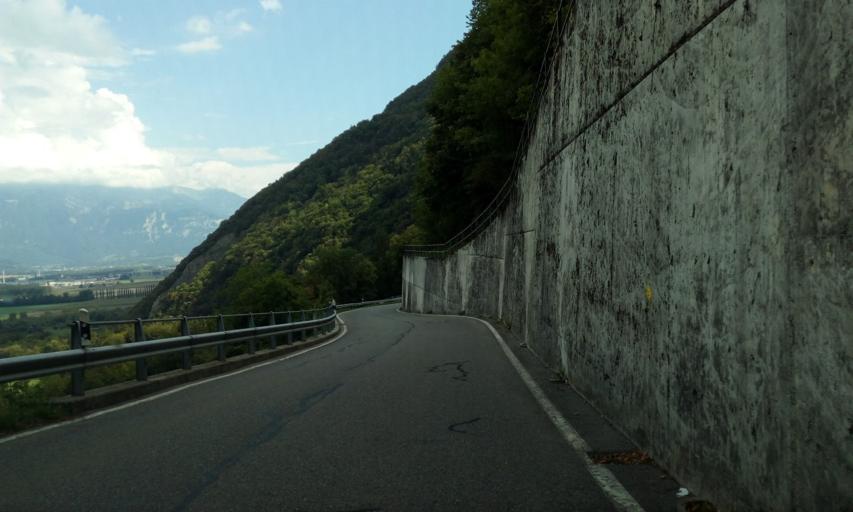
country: CH
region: Valais
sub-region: Monthey District
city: Vionnaz
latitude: 46.3094
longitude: 6.8960
